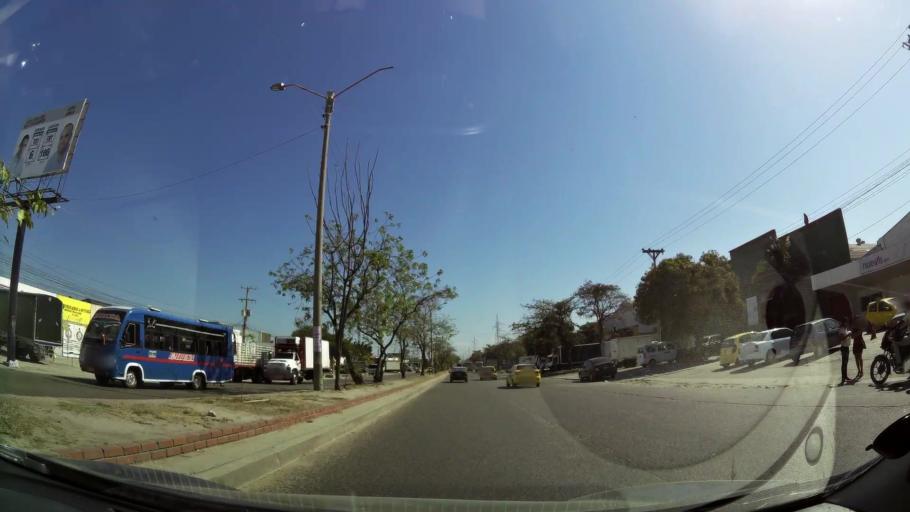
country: CO
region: Atlantico
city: Barranquilla
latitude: 10.9507
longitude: -74.7859
